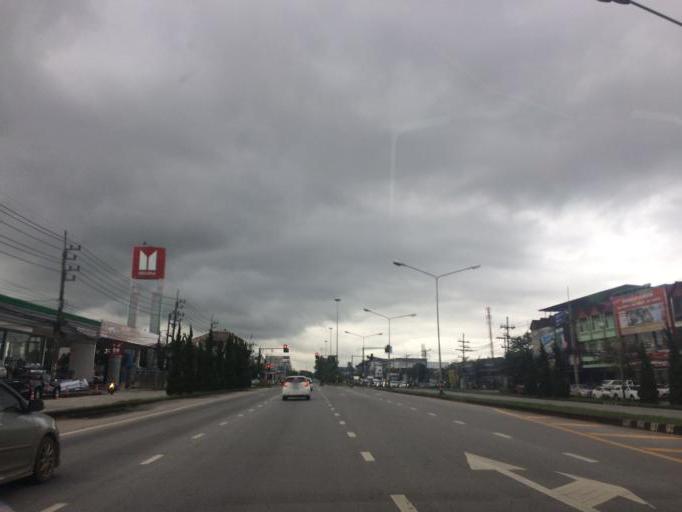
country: TH
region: Chiang Rai
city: Chiang Rai
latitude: 19.8971
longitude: 99.8386
